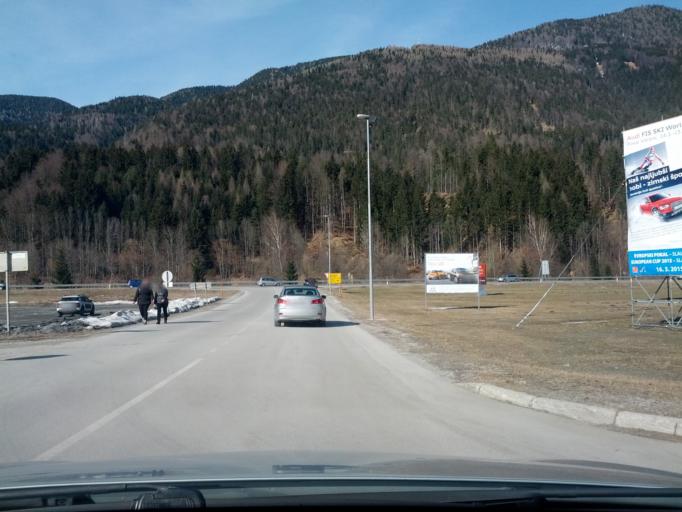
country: SI
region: Kranjska Gora
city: Kranjska Gora
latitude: 46.4870
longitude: 13.7790
